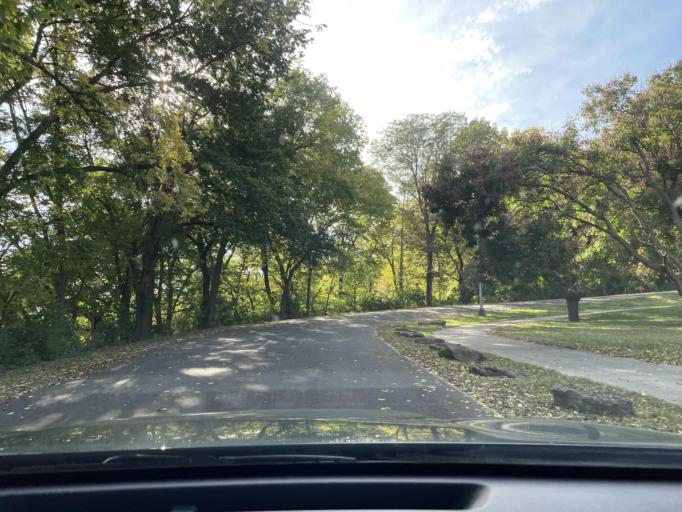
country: US
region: Kansas
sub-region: Doniphan County
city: Elwood
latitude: 39.7197
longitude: -94.8506
